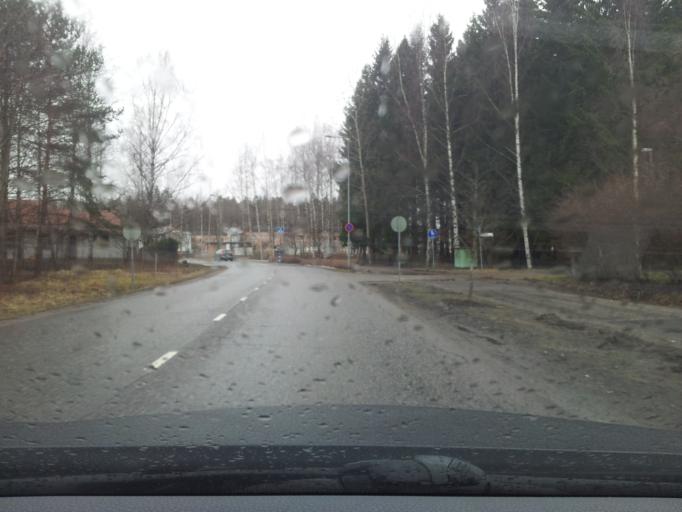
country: FI
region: Uusimaa
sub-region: Helsinki
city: Espoo
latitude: 60.1730
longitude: 24.6871
